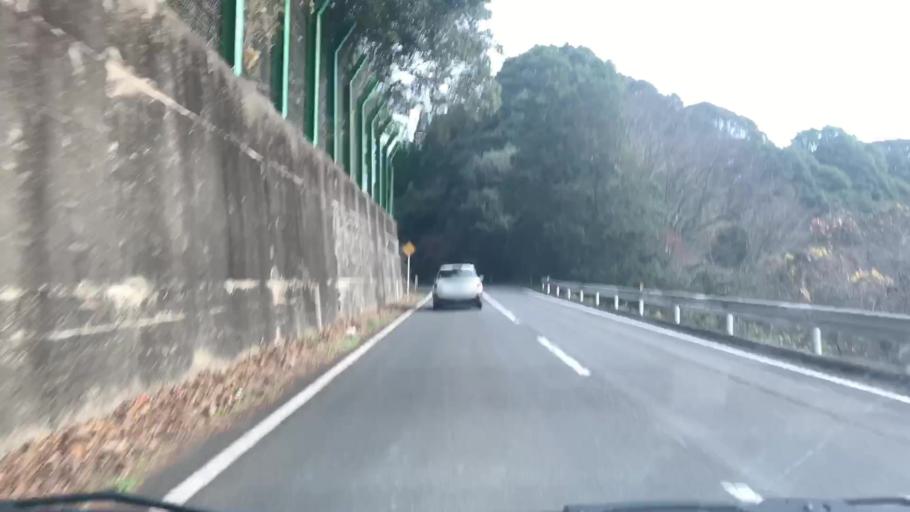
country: JP
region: Saga Prefecture
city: Imaricho-ko
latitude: 33.3290
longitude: 129.9694
